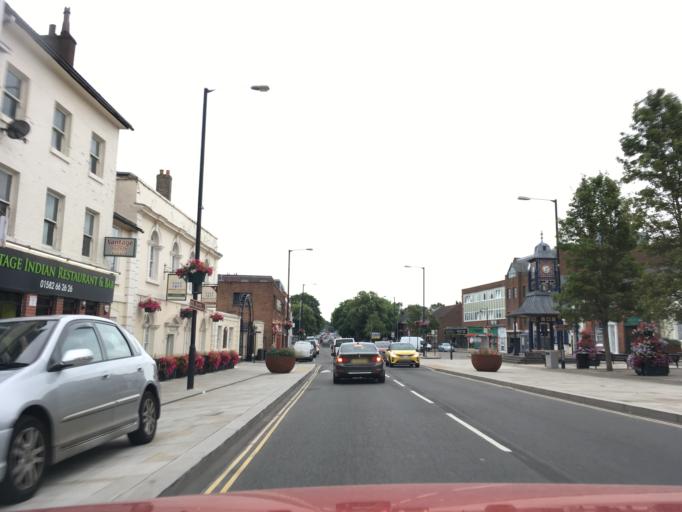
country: GB
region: England
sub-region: Central Bedfordshire
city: Dunstable
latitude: 51.8853
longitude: -0.5200
